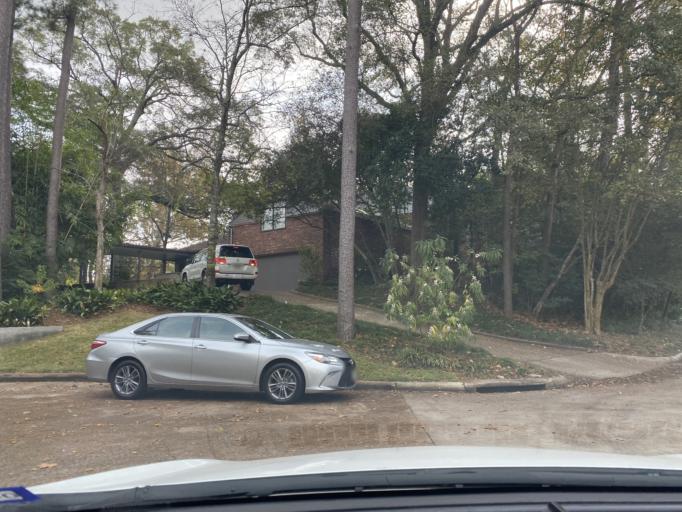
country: US
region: Texas
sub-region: Harris County
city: Hunters Creek Village
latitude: 29.7678
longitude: -95.4660
